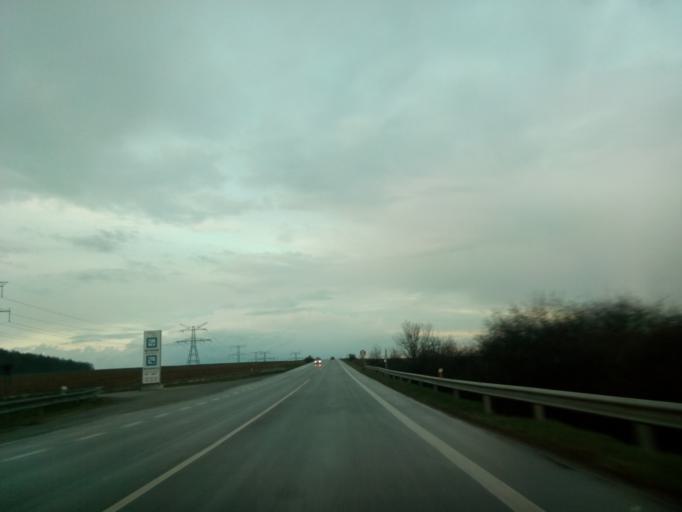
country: SK
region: Kosicky
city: Moldava nad Bodvou
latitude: 48.6084
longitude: 21.1153
